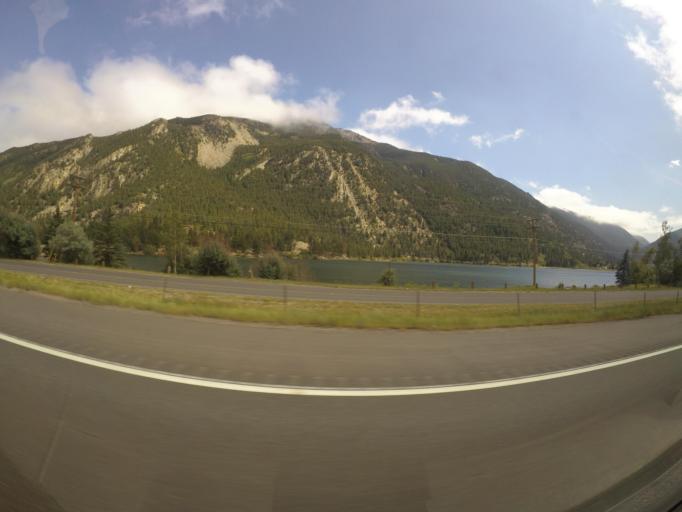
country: US
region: Colorado
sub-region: Clear Creek County
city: Georgetown
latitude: 39.7325
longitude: -105.6923
